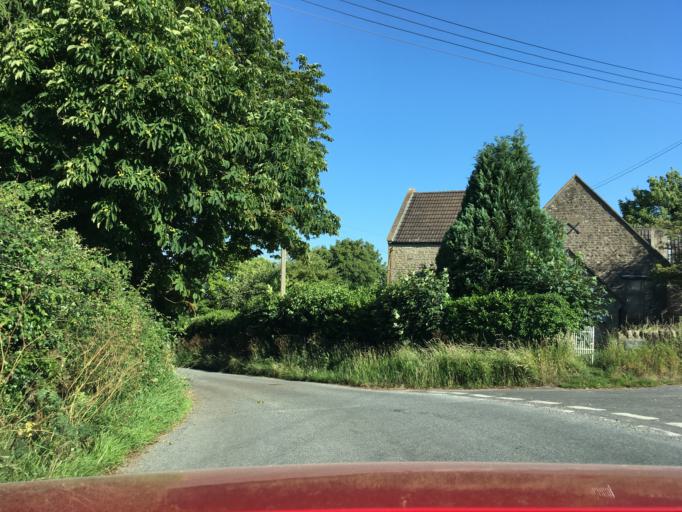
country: GB
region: England
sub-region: South Gloucestershire
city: Hinton
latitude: 51.4856
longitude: -2.3865
